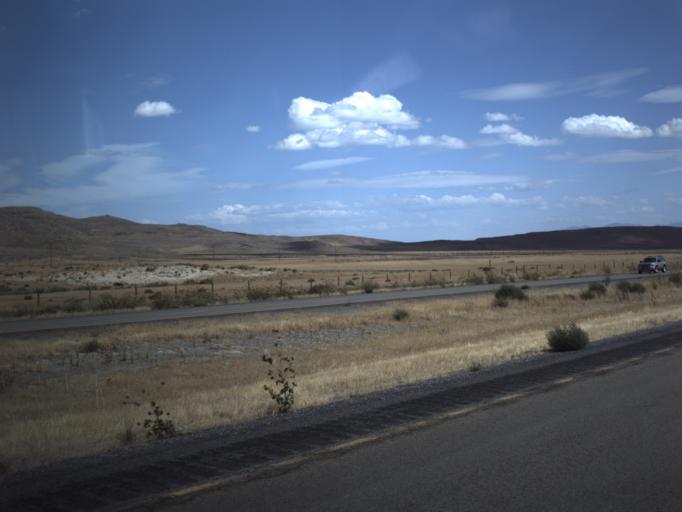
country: US
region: Utah
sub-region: Tooele County
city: Grantsville
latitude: 40.7955
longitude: -112.8415
